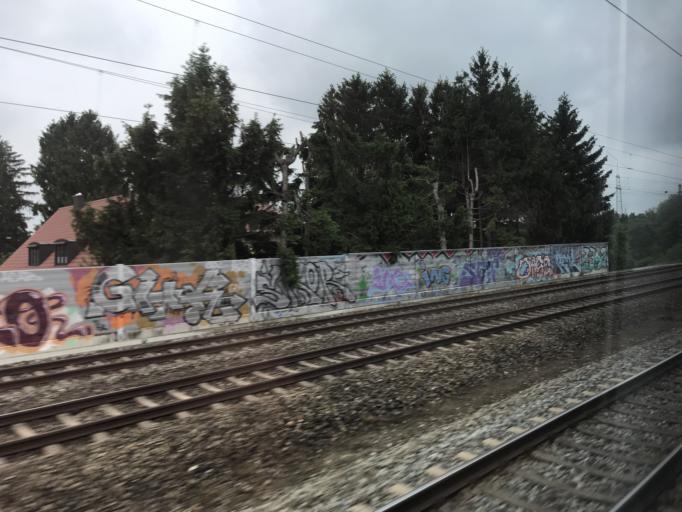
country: DE
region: Bavaria
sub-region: Upper Bavaria
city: Grobenzell
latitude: 48.1816
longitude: 11.3991
